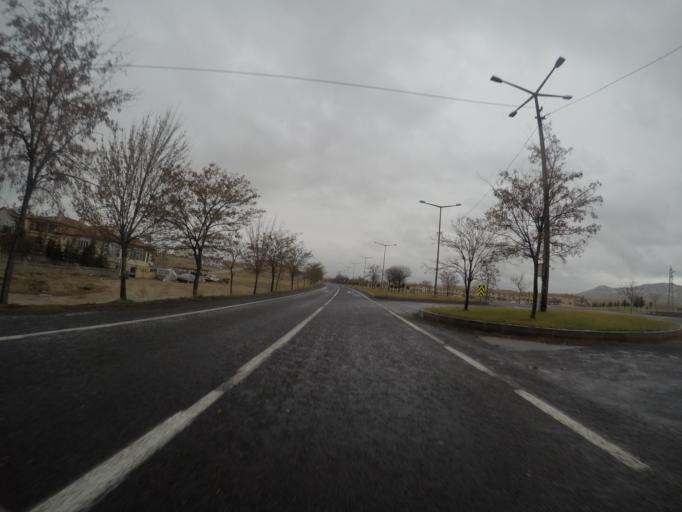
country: TR
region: Nevsehir
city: Avanos
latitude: 38.7011
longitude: 34.8607
